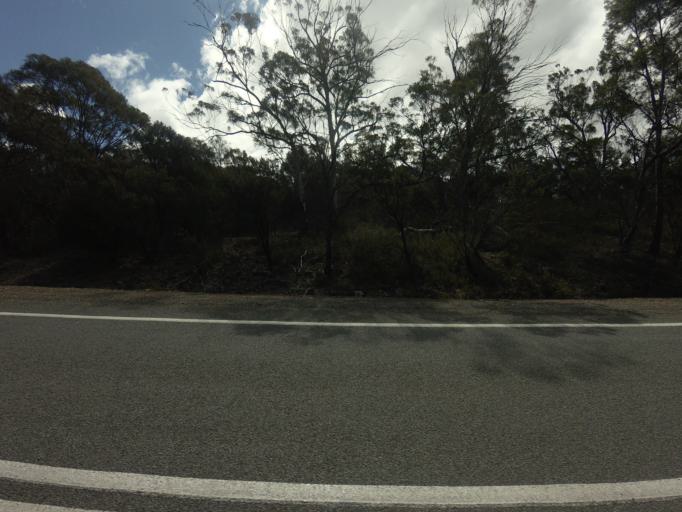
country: AU
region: Tasmania
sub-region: Break O'Day
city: St Helens
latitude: -42.0149
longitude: 147.9769
